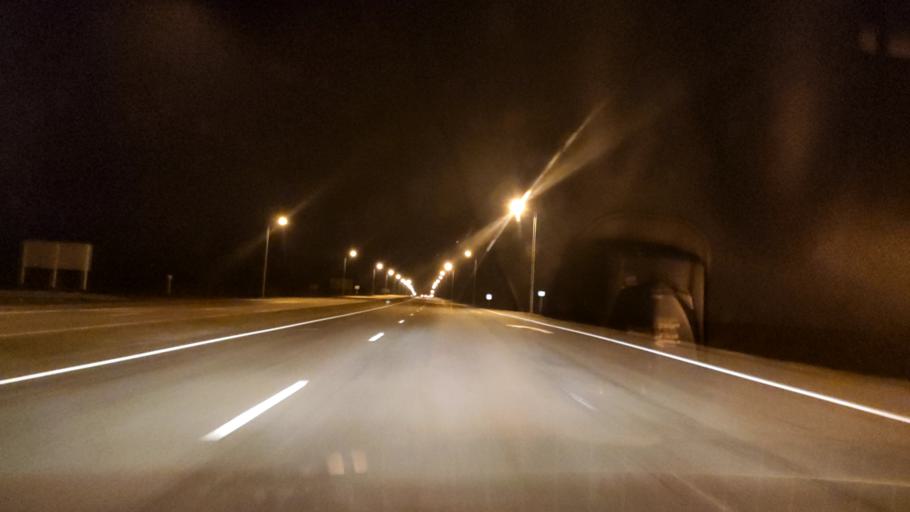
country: RU
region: Belgorod
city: Staryy Oskol
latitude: 51.3279
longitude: 37.7451
